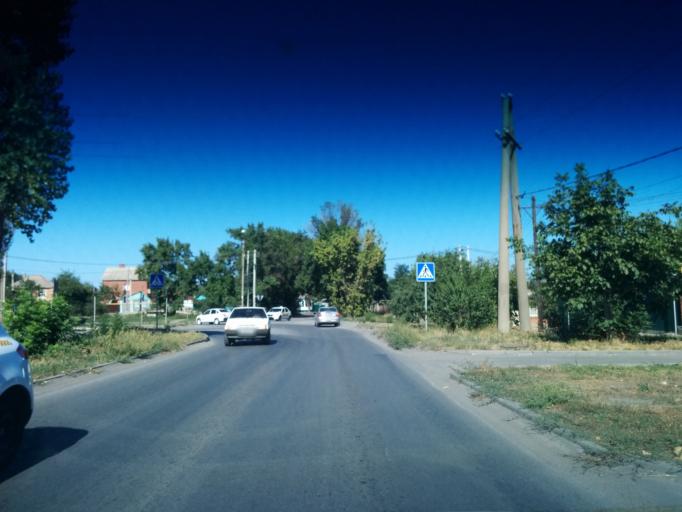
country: RU
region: Rostov
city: Shakhty
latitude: 47.7042
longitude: 40.2283
